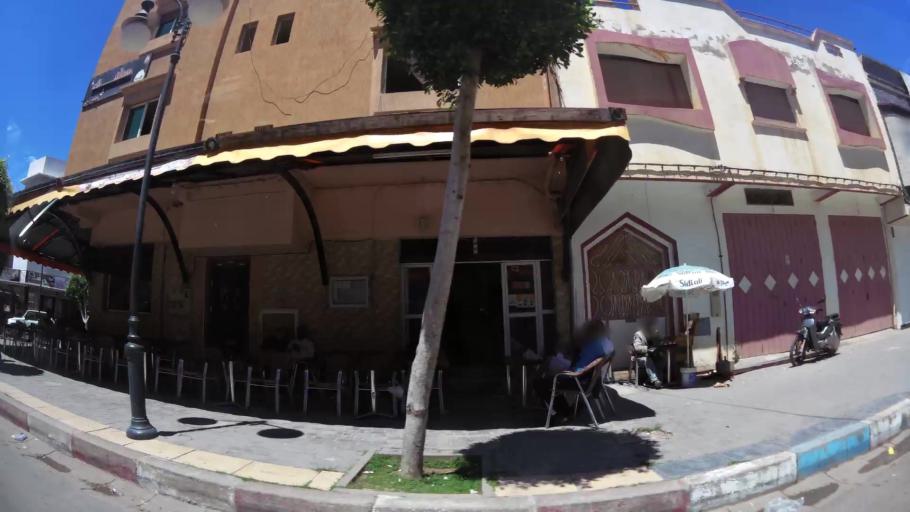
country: MA
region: Oriental
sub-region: Berkane-Taourirt
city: Madagh
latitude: 35.0783
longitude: -2.2253
